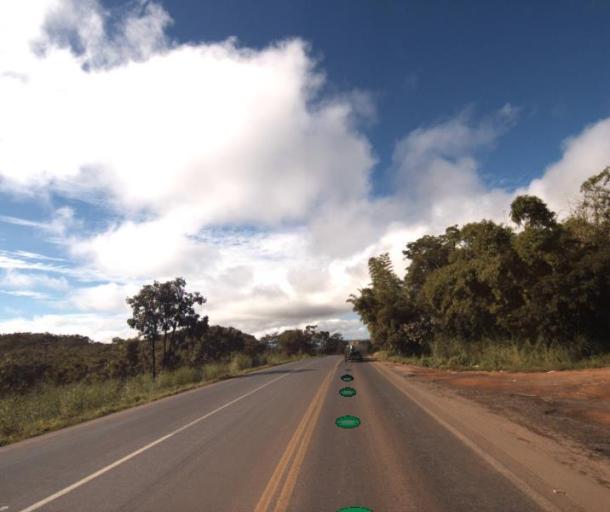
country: BR
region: Goias
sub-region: Uruacu
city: Uruacu
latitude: -14.5632
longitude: -49.1565
